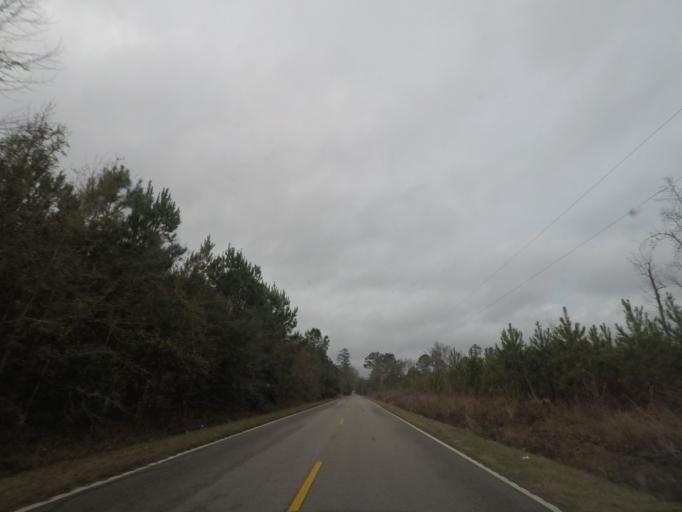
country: US
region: South Carolina
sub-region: Colleton County
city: Walterboro
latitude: 32.8760
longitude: -80.4931
